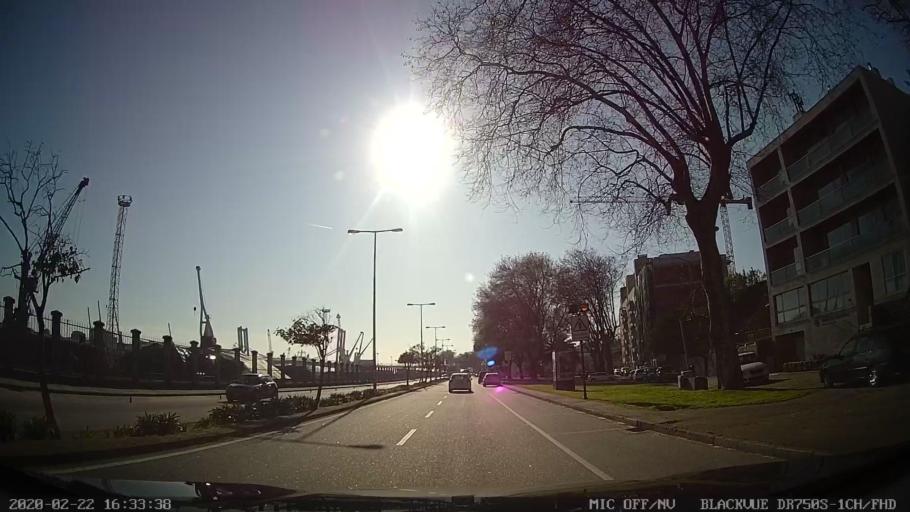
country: PT
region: Porto
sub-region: Matosinhos
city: Leca da Palmeira
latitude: 41.1921
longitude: -8.6915
